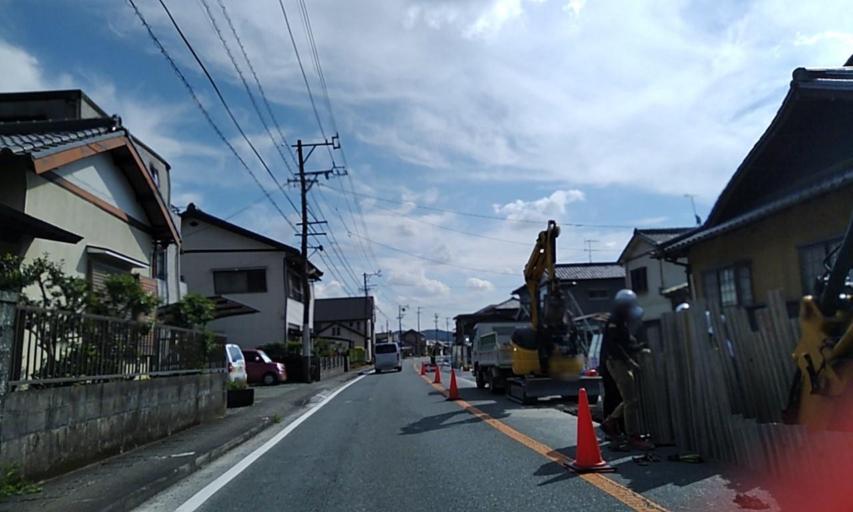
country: JP
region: Shizuoka
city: Hamakita
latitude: 34.8452
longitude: 137.8341
